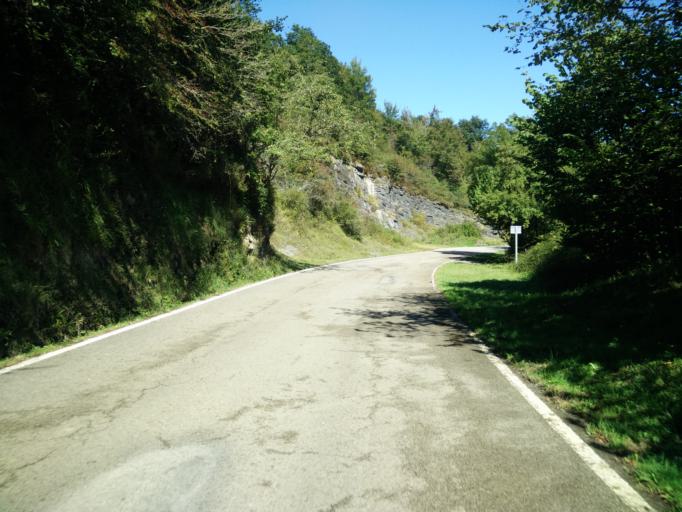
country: ES
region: Cantabria
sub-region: Provincia de Cantabria
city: Ruente
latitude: 43.1328
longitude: -4.2940
